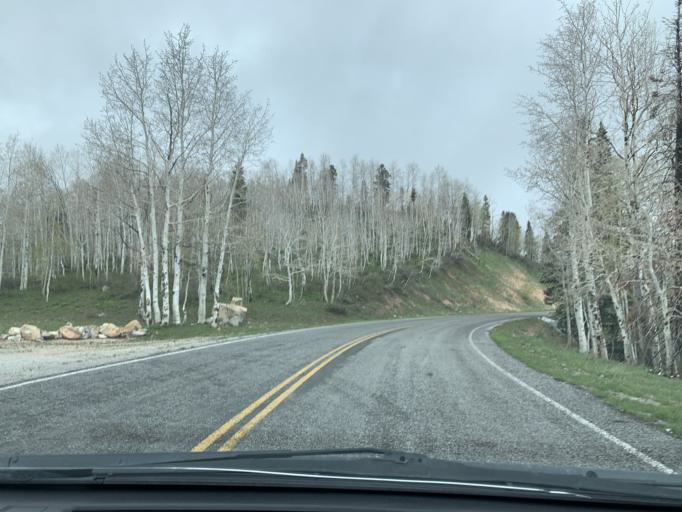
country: US
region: Utah
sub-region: Utah County
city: Elk Ridge
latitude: 39.8834
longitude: -111.6876
